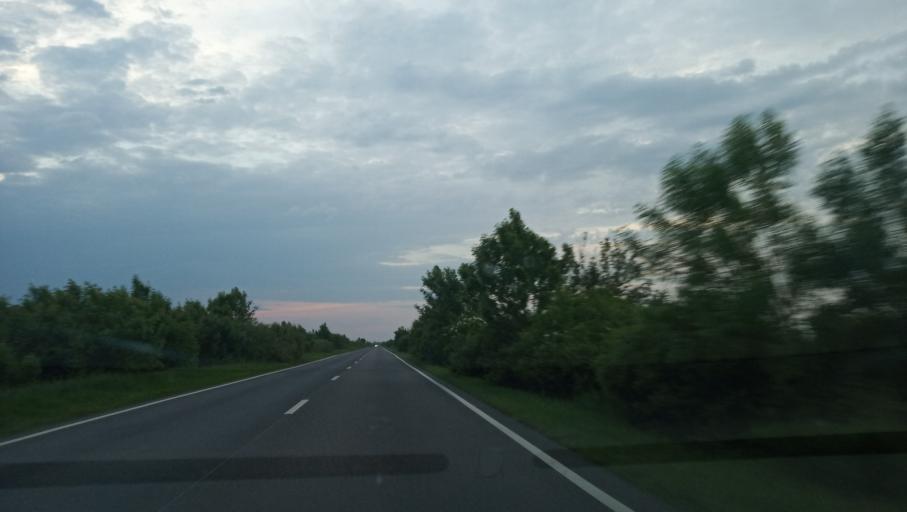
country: RO
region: Timis
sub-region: Comuna Jebel
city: Jebel
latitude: 45.5380
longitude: 21.2272
